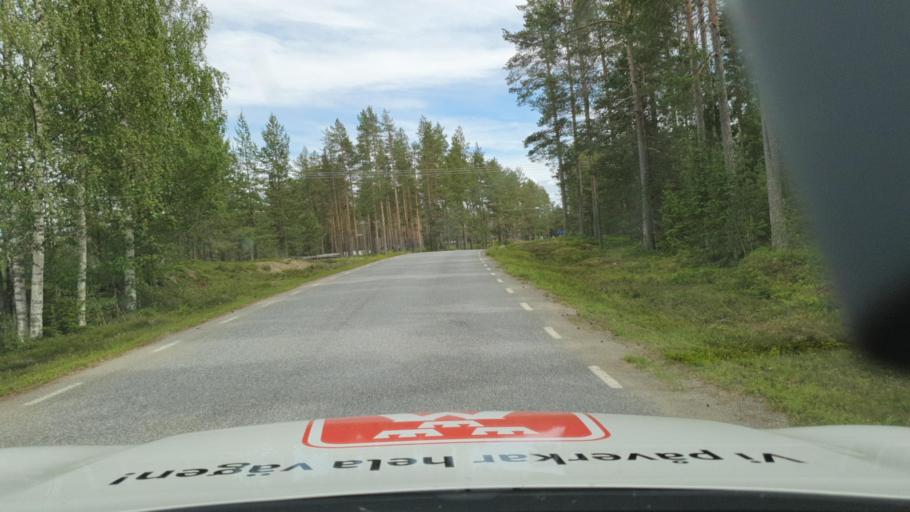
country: SE
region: Vaesterbotten
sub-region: Skelleftea Kommun
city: Burtraesk
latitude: 64.5005
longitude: 20.8472
